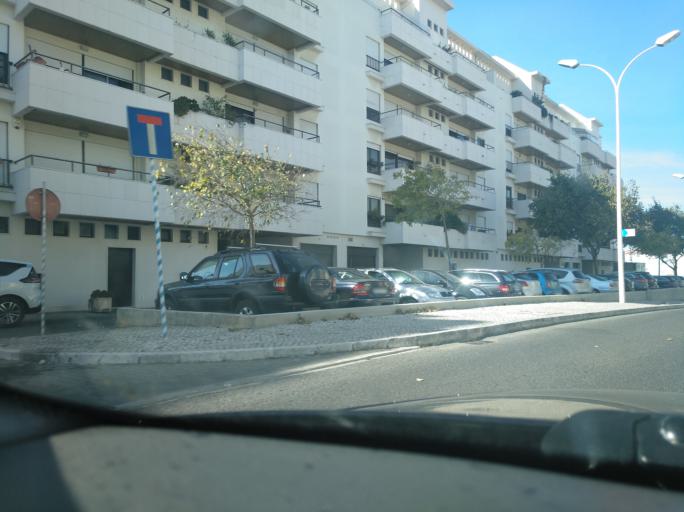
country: PT
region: Lisbon
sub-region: Oeiras
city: Alges
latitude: 38.7051
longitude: -9.2323
